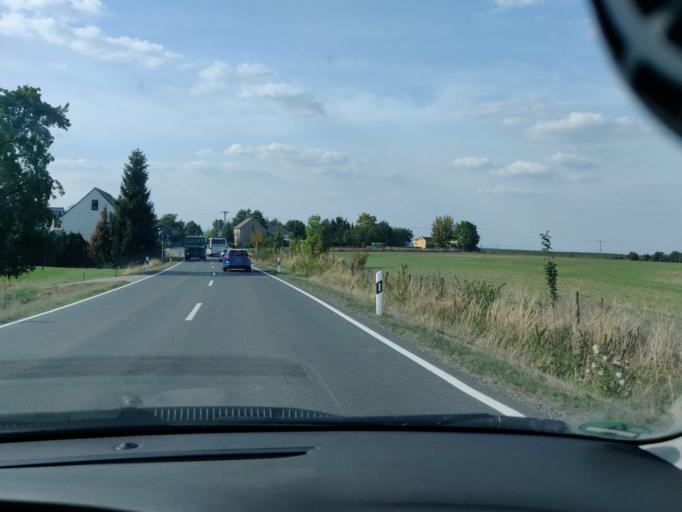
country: DE
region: Saxony
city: Seelitz
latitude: 51.0340
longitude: 12.8292
